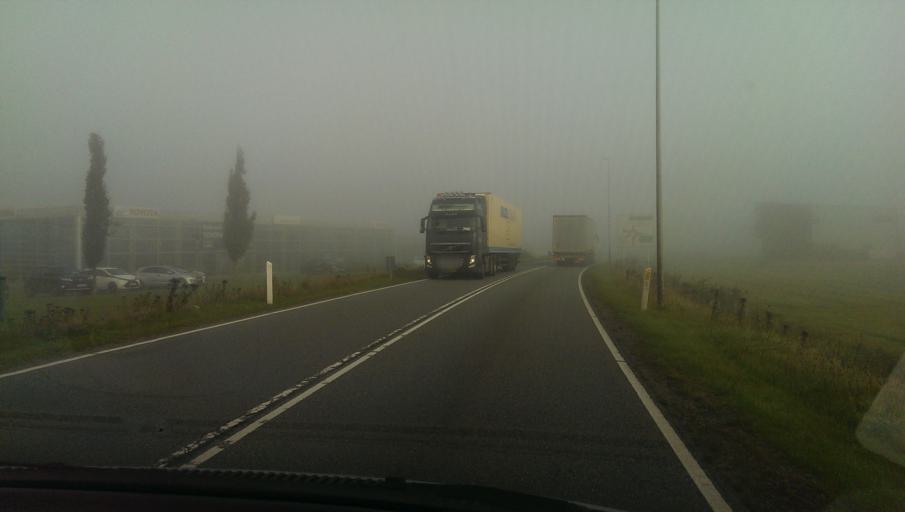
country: DK
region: South Denmark
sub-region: Vejen Kommune
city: Vejen
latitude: 55.4913
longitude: 9.1301
